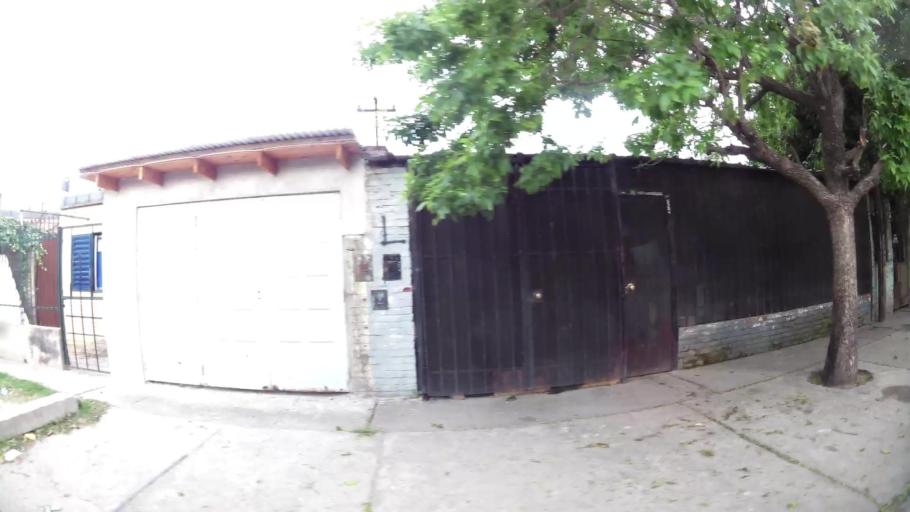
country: AR
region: Santa Fe
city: Gobernador Galvez
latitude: -33.0002
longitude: -60.6882
